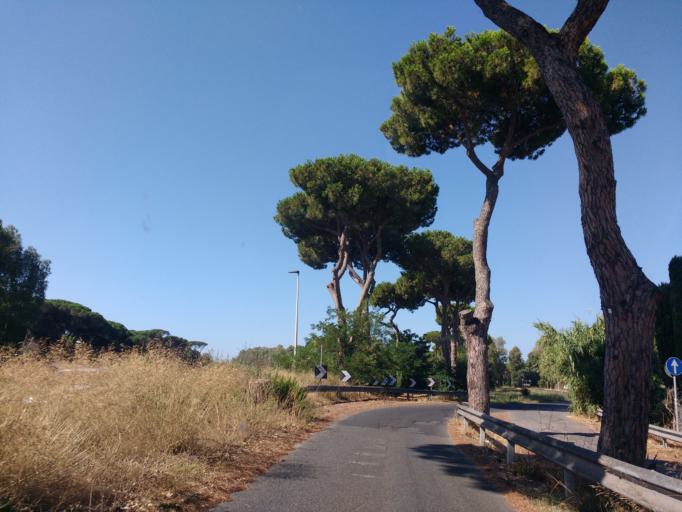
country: IT
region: Latium
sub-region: Citta metropolitana di Roma Capitale
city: Acilia-Castel Fusano-Ostia Antica
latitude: 41.7453
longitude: 12.3225
